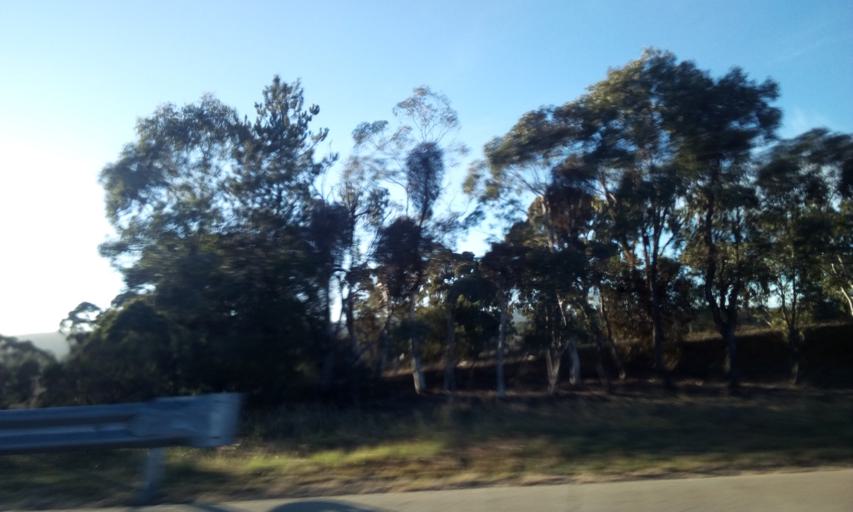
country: AU
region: New South Wales
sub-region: Yass Valley
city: Gundaroo
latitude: -35.1351
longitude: 149.3398
